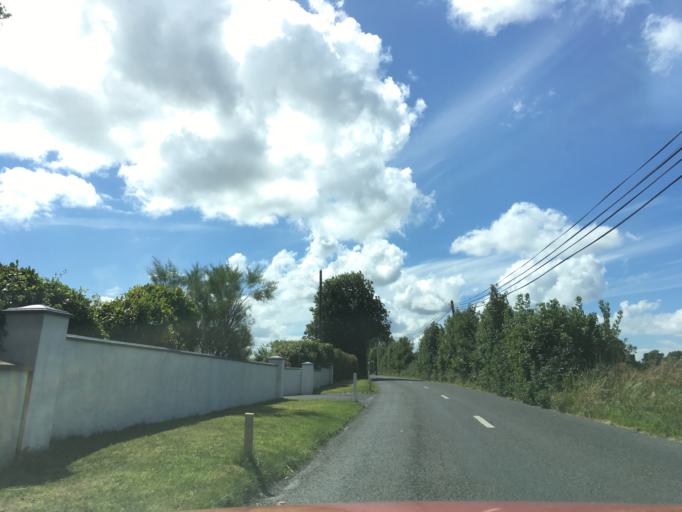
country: IE
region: Munster
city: Cahir
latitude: 52.3416
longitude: -7.9552
